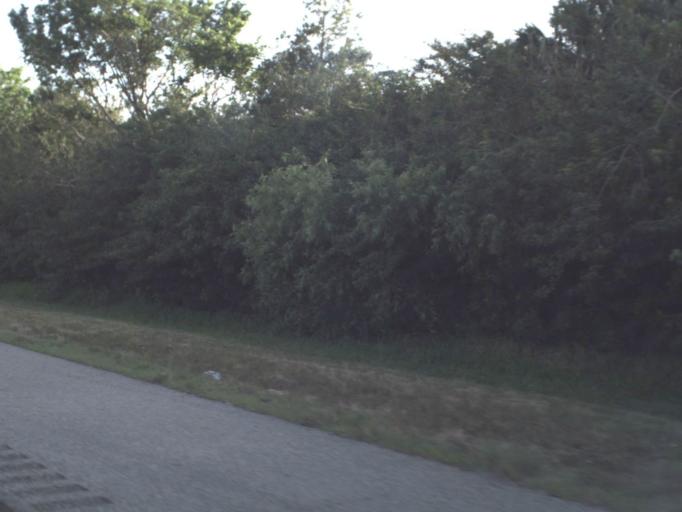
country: US
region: Florida
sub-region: Brevard County
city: Titusville
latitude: 28.5833
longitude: -80.8516
